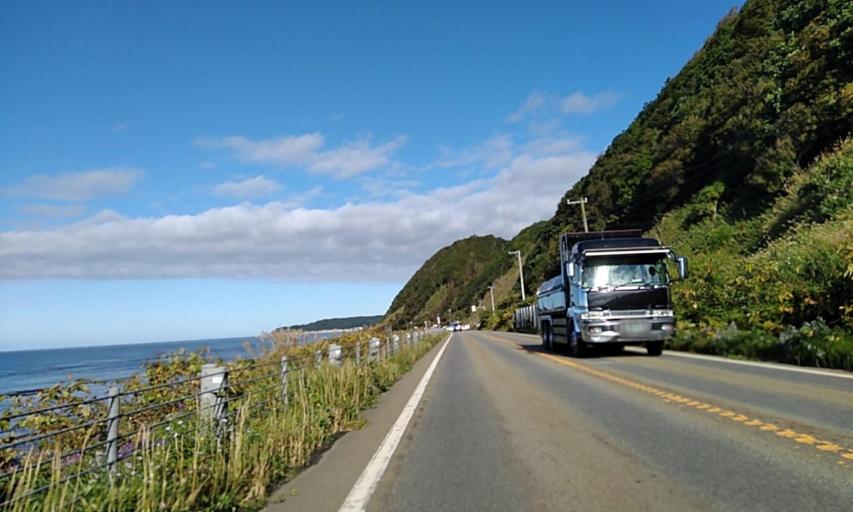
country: JP
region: Hokkaido
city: Shizunai-furukawacho
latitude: 42.2573
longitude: 142.5303
